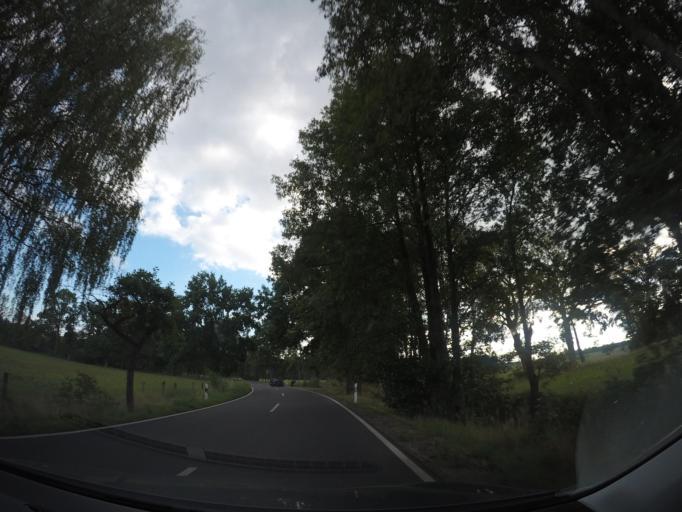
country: DE
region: Saxony-Anhalt
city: Mieste
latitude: 52.4954
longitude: 11.1322
